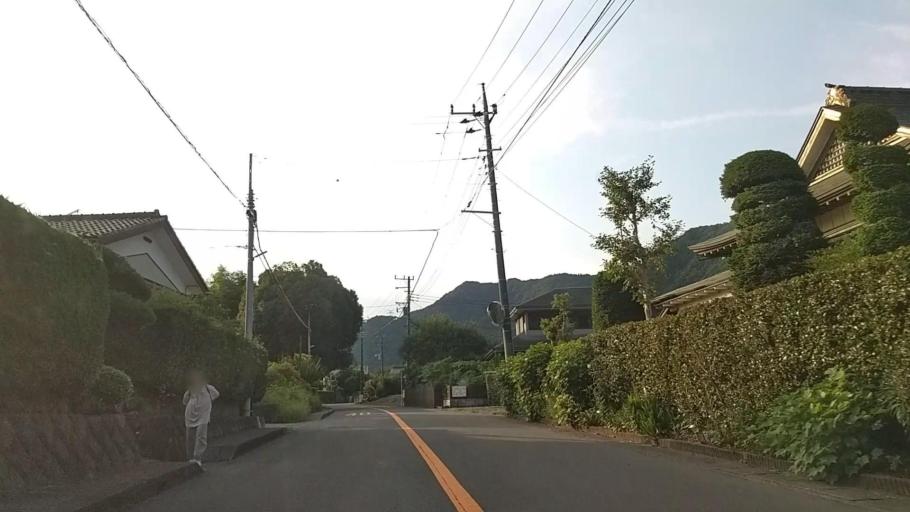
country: JP
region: Tokyo
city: Hachioji
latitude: 35.5922
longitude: 139.2480
